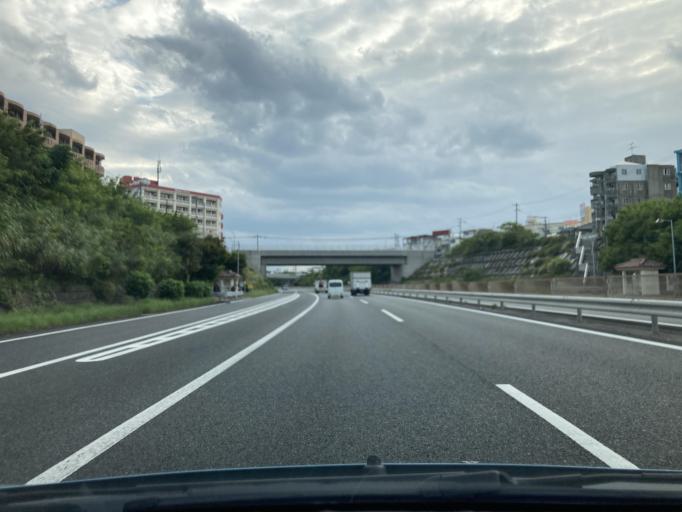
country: JP
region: Okinawa
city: Ginowan
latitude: 26.2559
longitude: 127.7641
